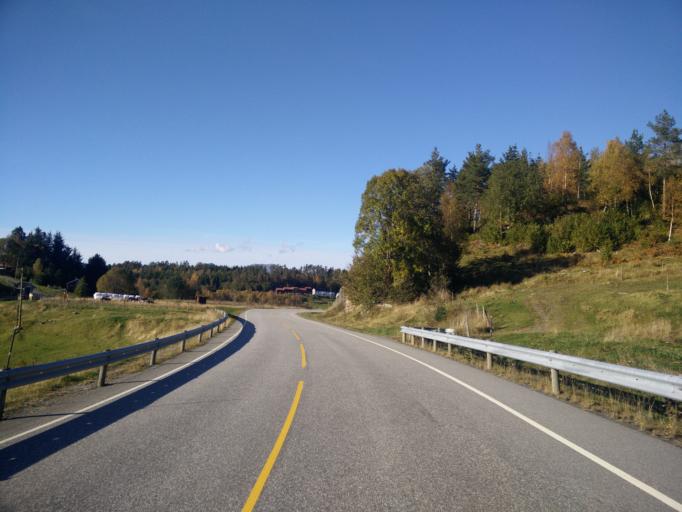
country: NO
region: More og Romsdal
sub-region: Halsa
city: Liaboen
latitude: 63.0974
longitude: 8.3447
